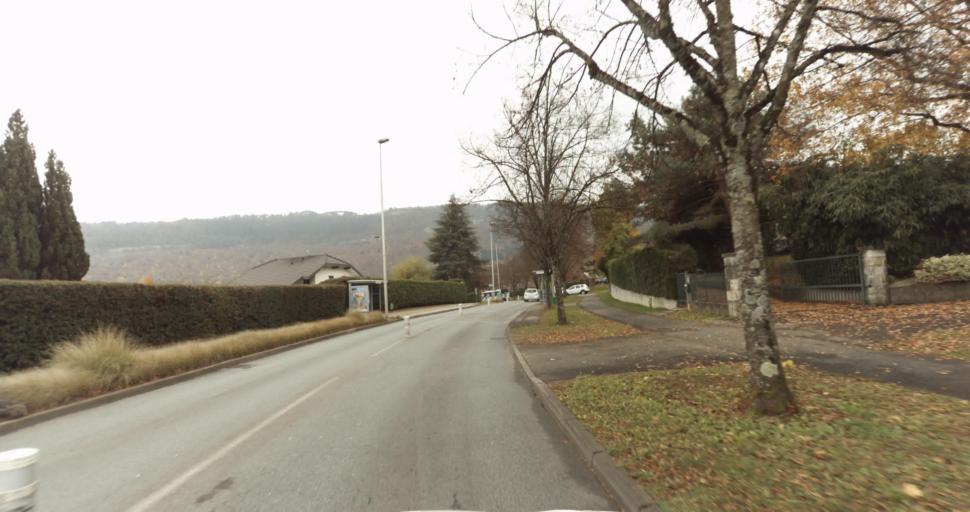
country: FR
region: Rhone-Alpes
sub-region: Departement de la Haute-Savoie
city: Cran-Gevrier
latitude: 45.8837
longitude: 6.1056
